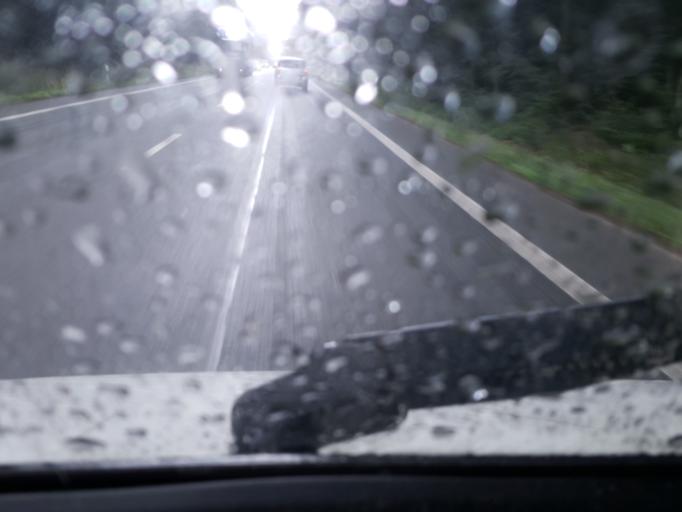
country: DE
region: North Rhine-Westphalia
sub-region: Regierungsbezirk Detmold
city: Petershagen
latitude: 52.3462
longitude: 8.9452
